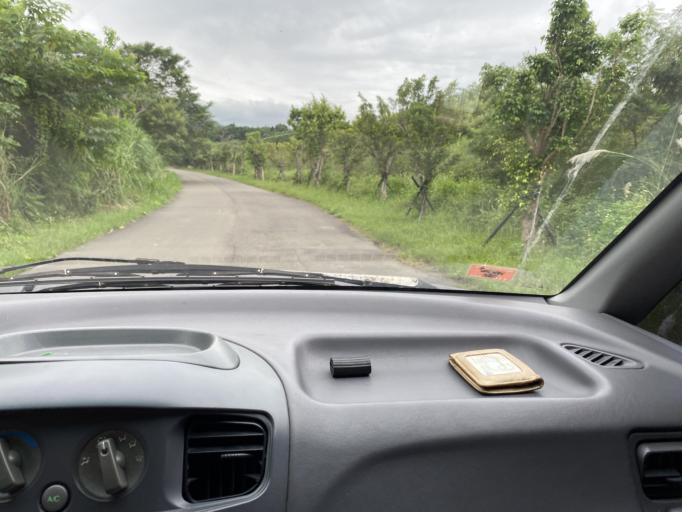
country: TW
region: Taiwan
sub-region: Hsinchu
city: Zhubei
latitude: 24.7180
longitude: 121.1029
